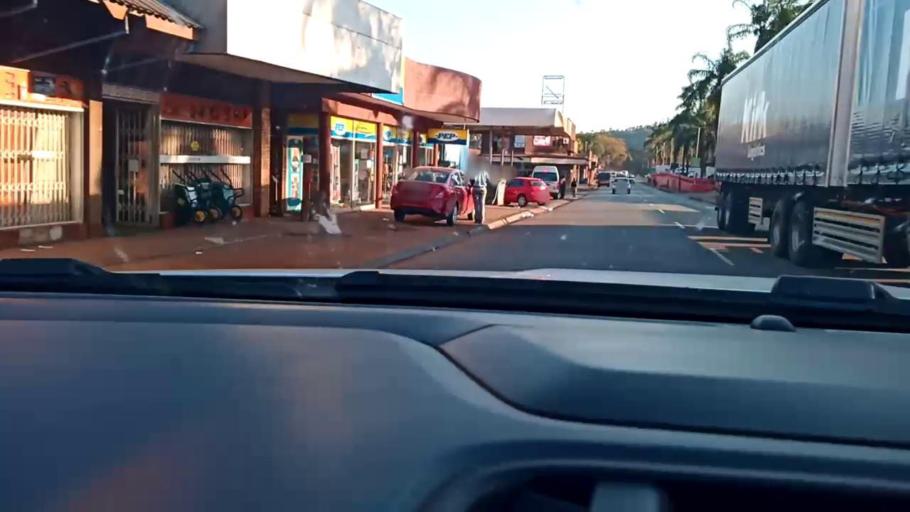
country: ZA
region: Limpopo
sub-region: Mopani District Municipality
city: Duiwelskloof
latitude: -23.6964
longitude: 30.1402
